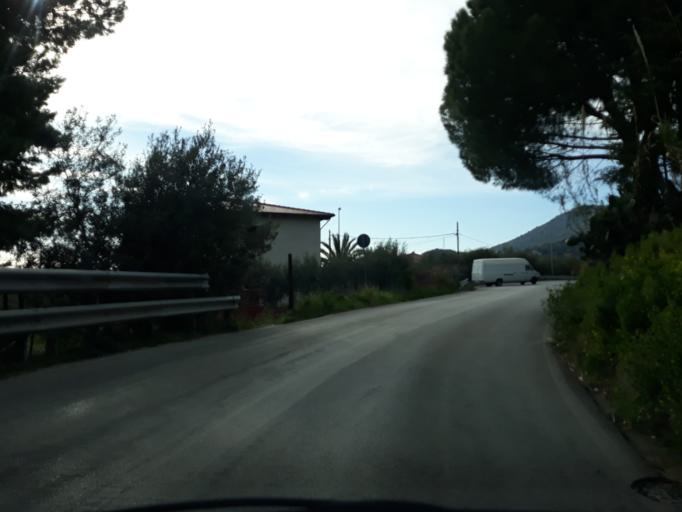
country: IT
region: Sicily
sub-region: Palermo
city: Montelepre
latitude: 38.0880
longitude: 13.1662
